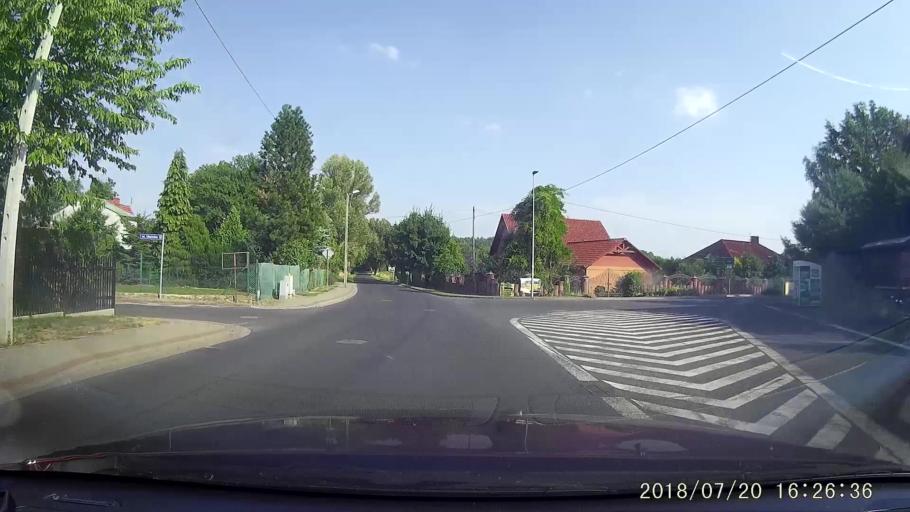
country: PL
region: Lower Silesian Voivodeship
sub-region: Powiat zgorzelecki
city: Lagow
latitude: 51.1295
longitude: 15.0376
